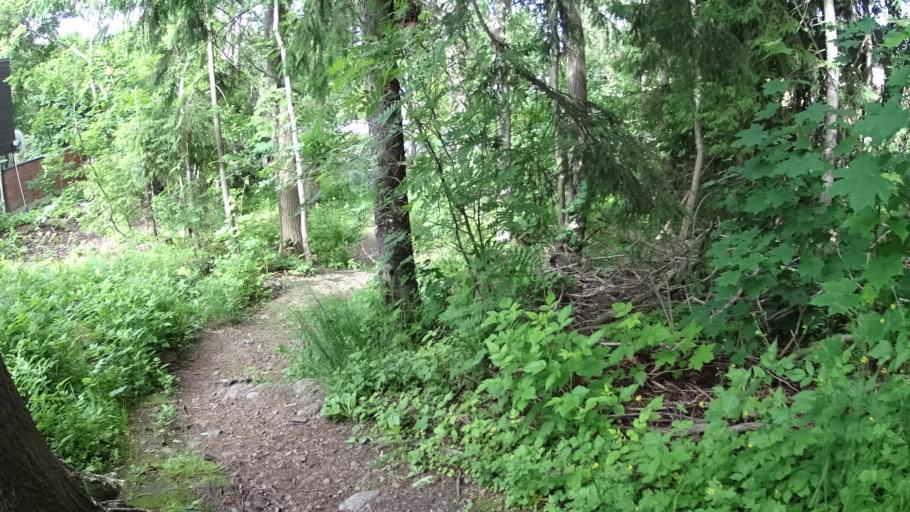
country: FI
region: Uusimaa
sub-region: Helsinki
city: Koukkuniemi
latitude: 60.1716
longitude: 24.7872
